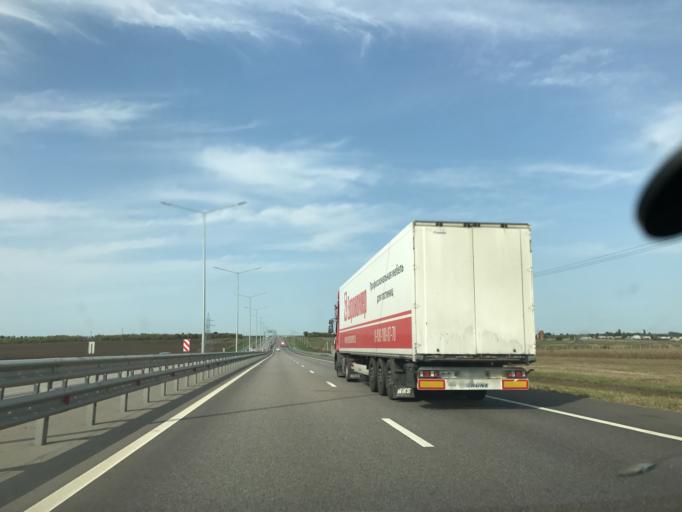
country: RU
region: Voronezj
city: Kashirskoye
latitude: 51.4897
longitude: 39.5318
